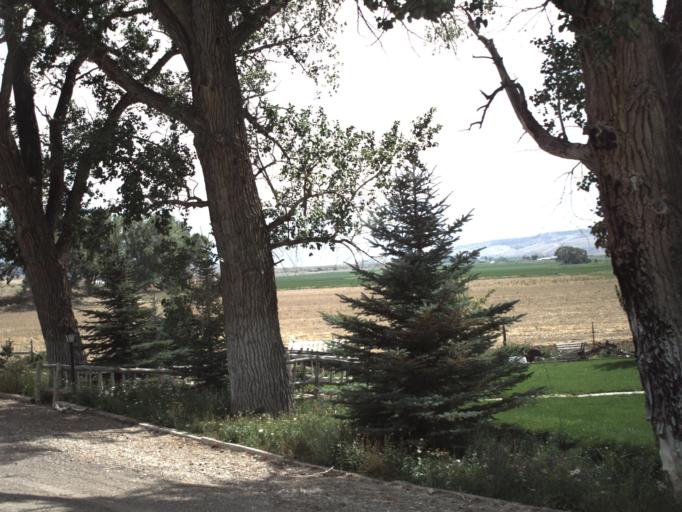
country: US
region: Utah
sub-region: Piute County
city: Junction
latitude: 38.1547
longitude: -112.0048
